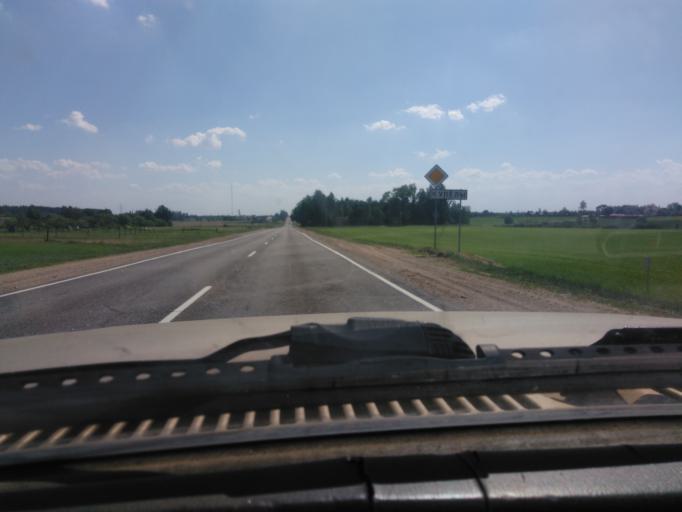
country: BY
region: Mogilev
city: Kamyennyya Lavy
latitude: 54.0380
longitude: 30.3243
